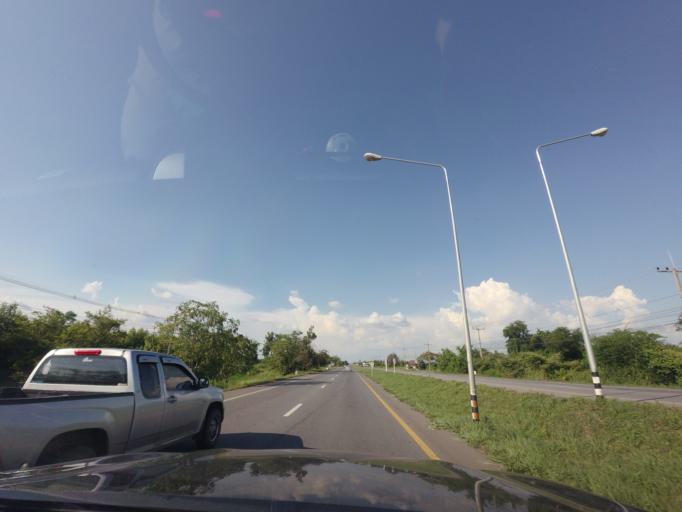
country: TH
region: Khon Kaen
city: Non Sila
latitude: 15.9851
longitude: 102.6971
